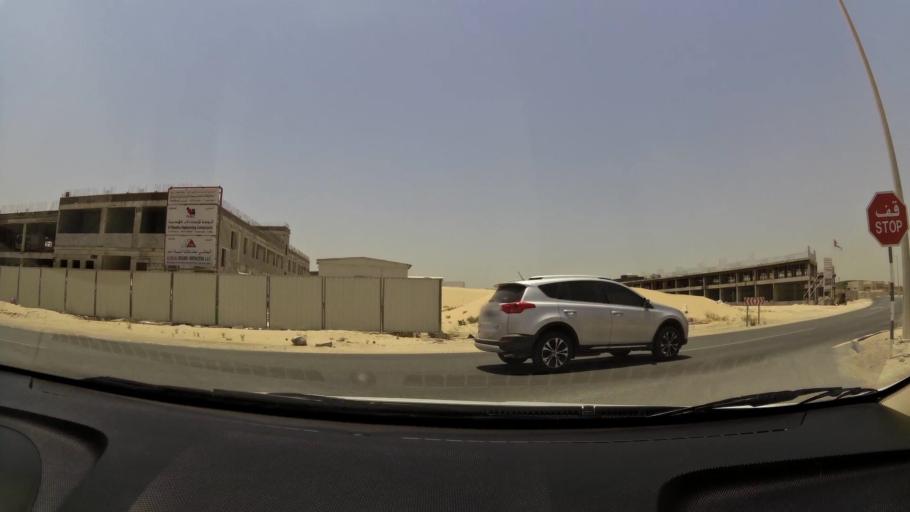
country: AE
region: Ajman
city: Ajman
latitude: 25.4043
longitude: 55.4995
